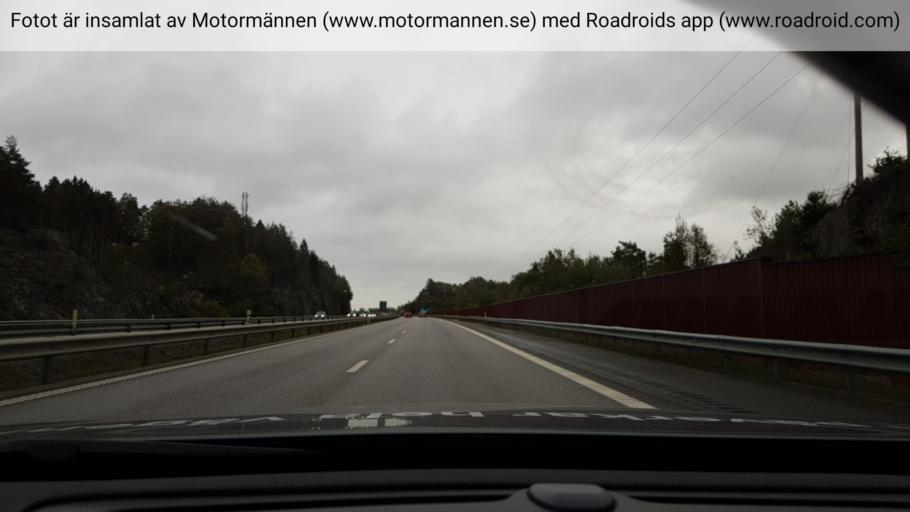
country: SE
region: Vaestra Goetaland
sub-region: Harryda Kommun
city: Molnlycke
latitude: 57.6795
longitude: 12.1549
